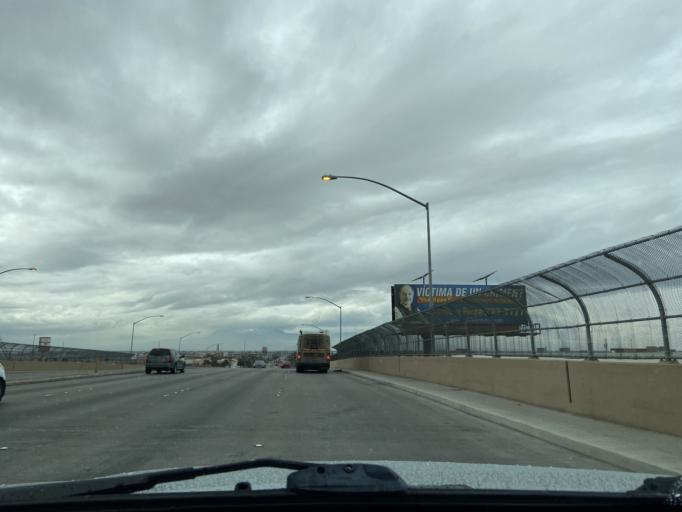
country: US
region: Nevada
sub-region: Clark County
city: North Las Vegas
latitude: 36.2401
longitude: -115.1064
